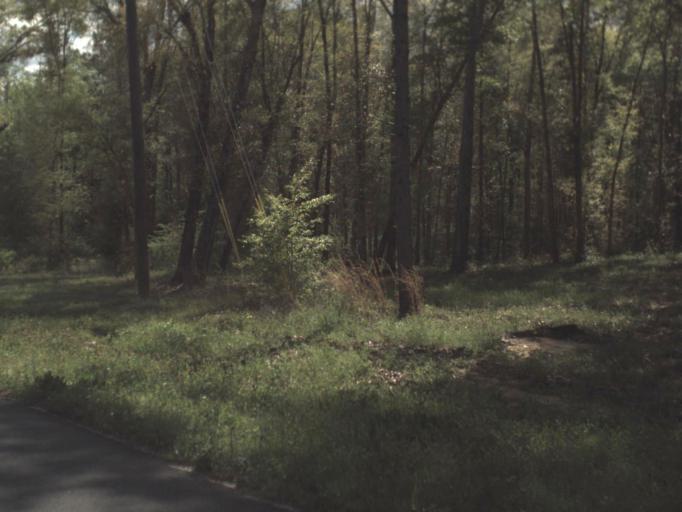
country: US
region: Florida
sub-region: Okaloosa County
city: Crestview
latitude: 30.8851
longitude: -86.5068
